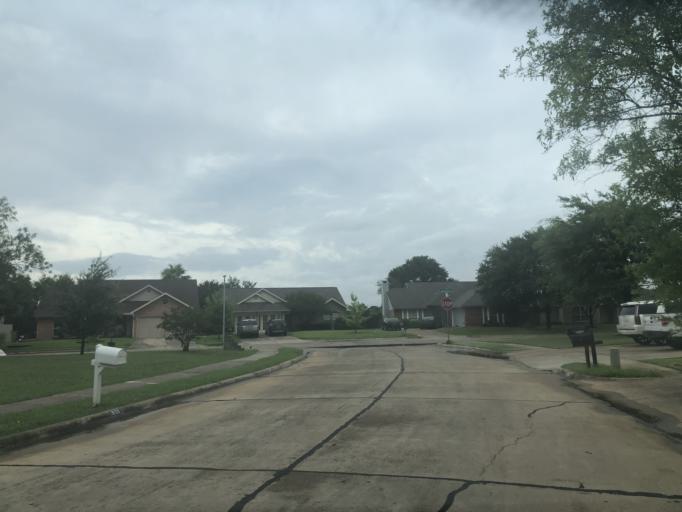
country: US
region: Texas
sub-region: Dallas County
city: Irving
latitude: 32.7863
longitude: -96.9639
